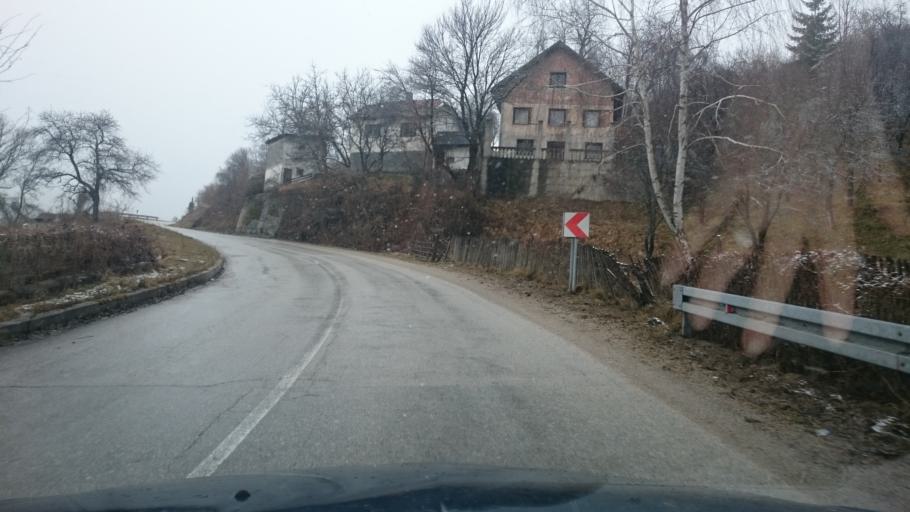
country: BA
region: Federation of Bosnia and Herzegovina
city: Turbe
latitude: 44.2621
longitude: 17.5442
